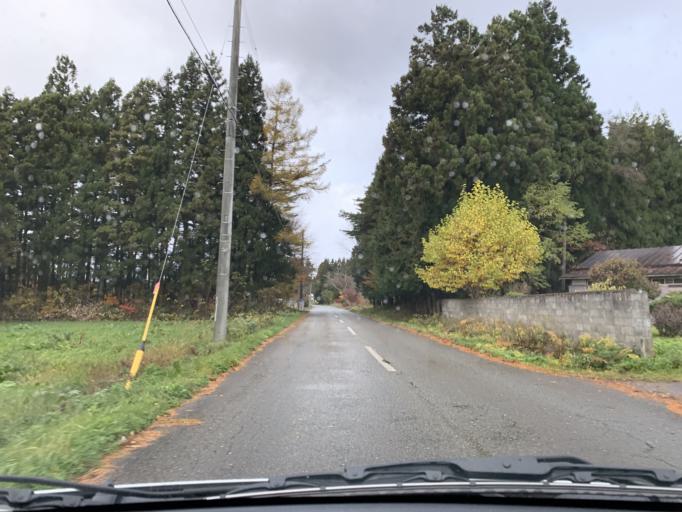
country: JP
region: Iwate
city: Mizusawa
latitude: 39.0928
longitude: 140.9938
